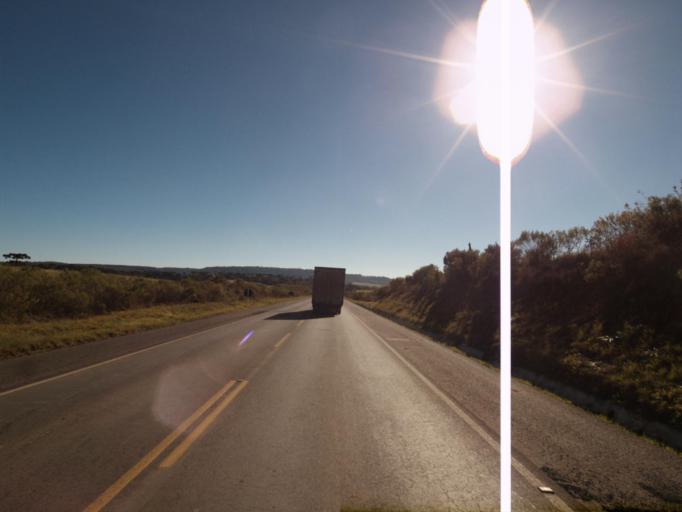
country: BR
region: Santa Catarina
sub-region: Concordia
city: Concordia
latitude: -26.9455
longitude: -51.8241
